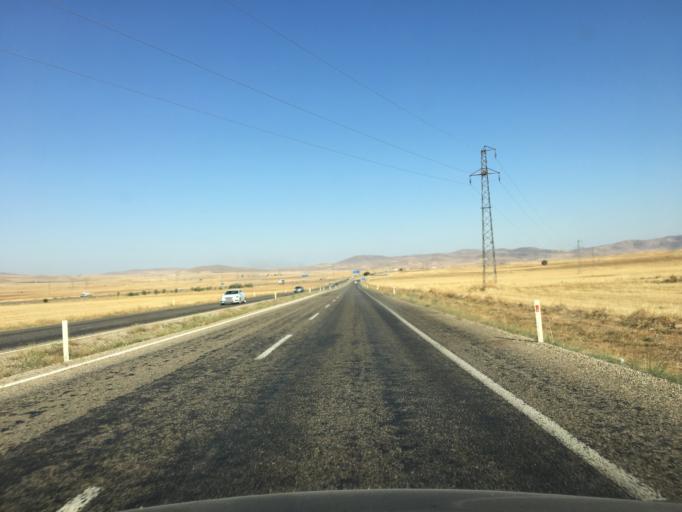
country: TR
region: Kirsehir
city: Akpinar
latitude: 39.3293
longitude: 34.0281
